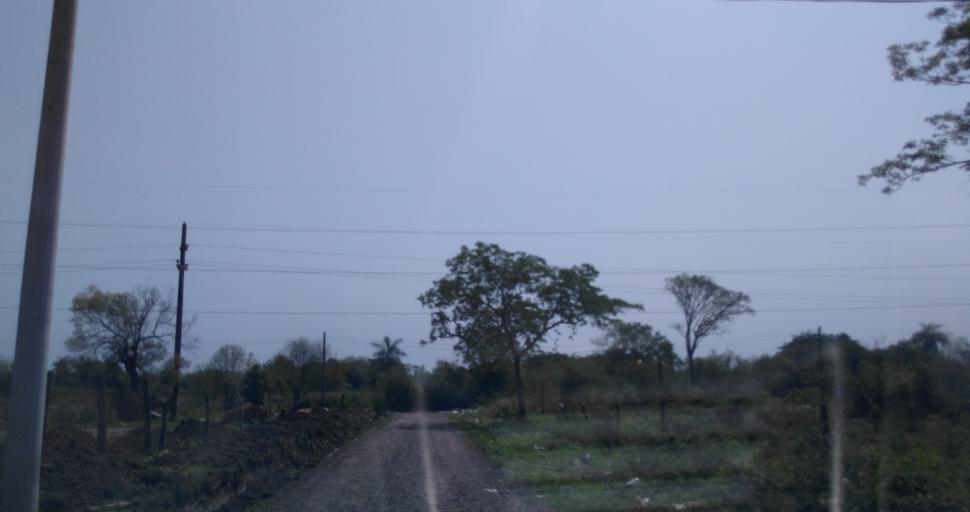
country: AR
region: Chaco
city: Fontana
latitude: -27.4158
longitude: -59.0196
